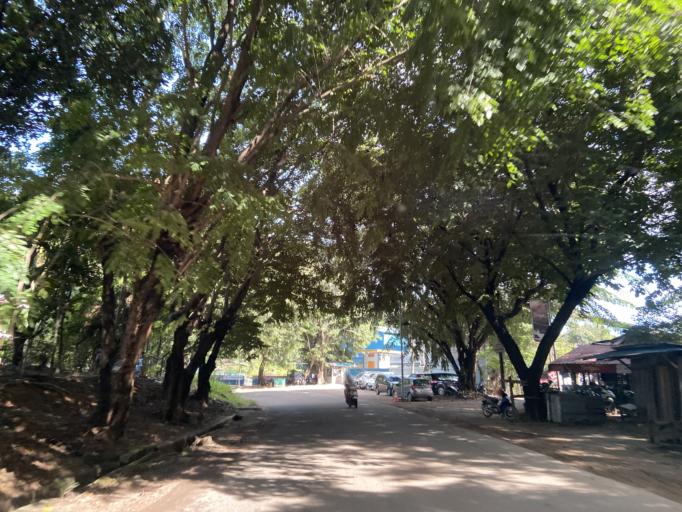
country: SG
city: Singapore
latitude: 1.1785
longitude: 104.0093
